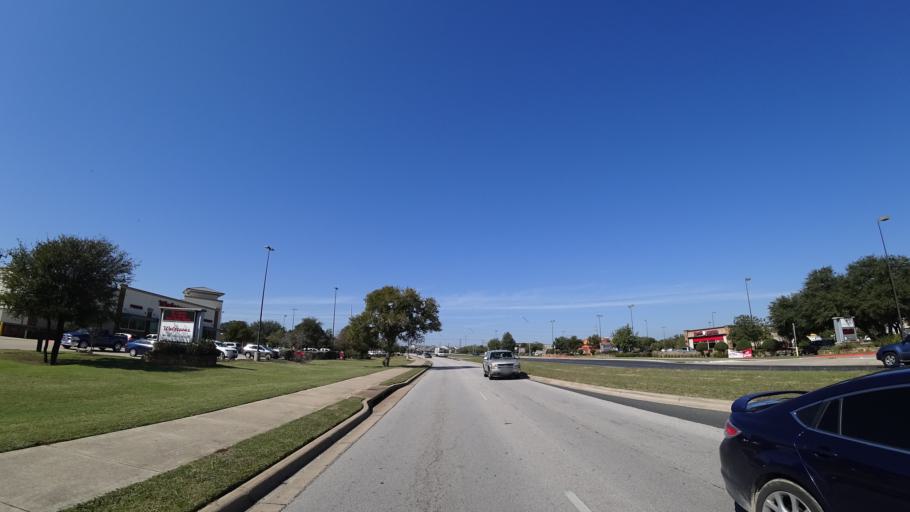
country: US
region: Texas
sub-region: Travis County
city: Shady Hollow
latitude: 30.1993
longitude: -97.8635
